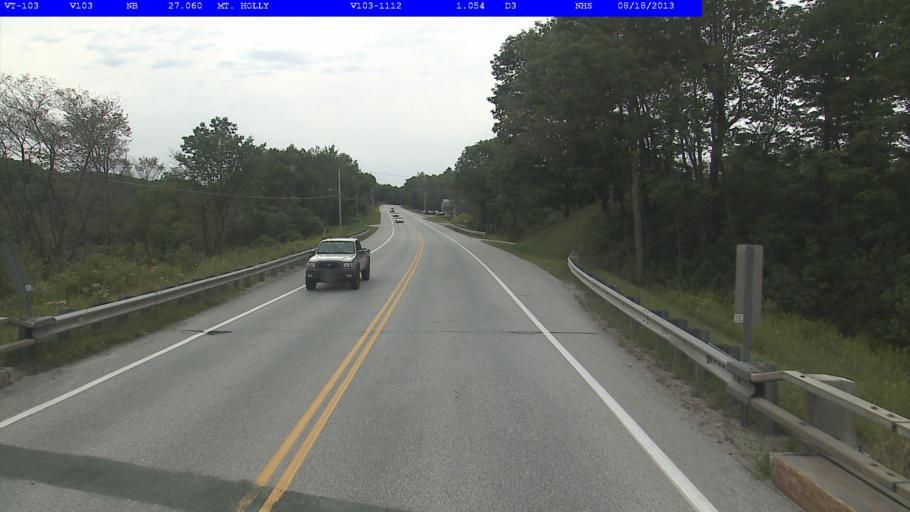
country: US
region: Vermont
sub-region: Windsor County
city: Chester
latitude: 43.4376
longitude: -72.7535
